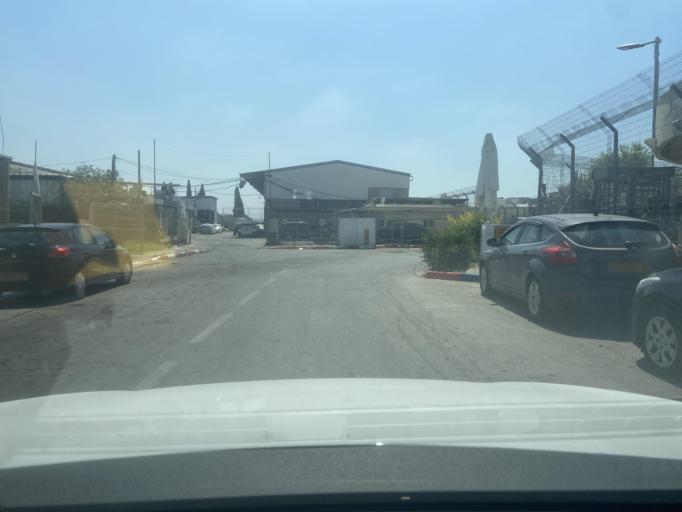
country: IL
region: Central District
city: Yehud
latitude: 32.0310
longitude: 34.9002
